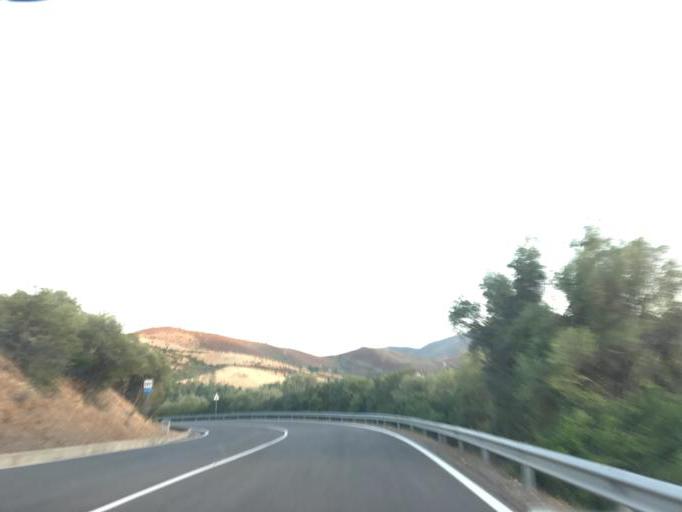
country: IT
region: Sardinia
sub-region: Provincia di Olbia-Tempio
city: San Teodoro
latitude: 40.7320
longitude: 9.6493
